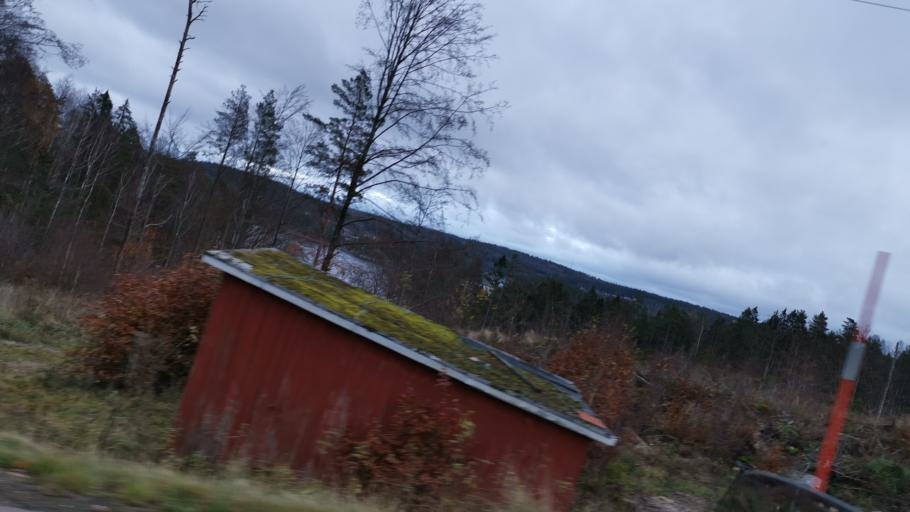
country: SE
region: Vaestra Goetaland
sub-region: Orust
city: Henan
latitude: 58.2984
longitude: 11.6615
